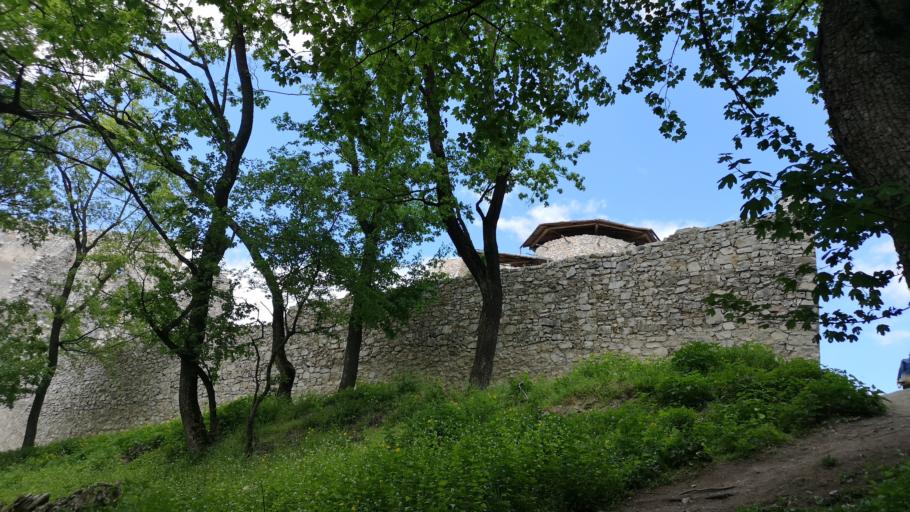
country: SK
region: Nitriansky
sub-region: Okres Nitra
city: Nitra
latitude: 48.4478
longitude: 18.1564
